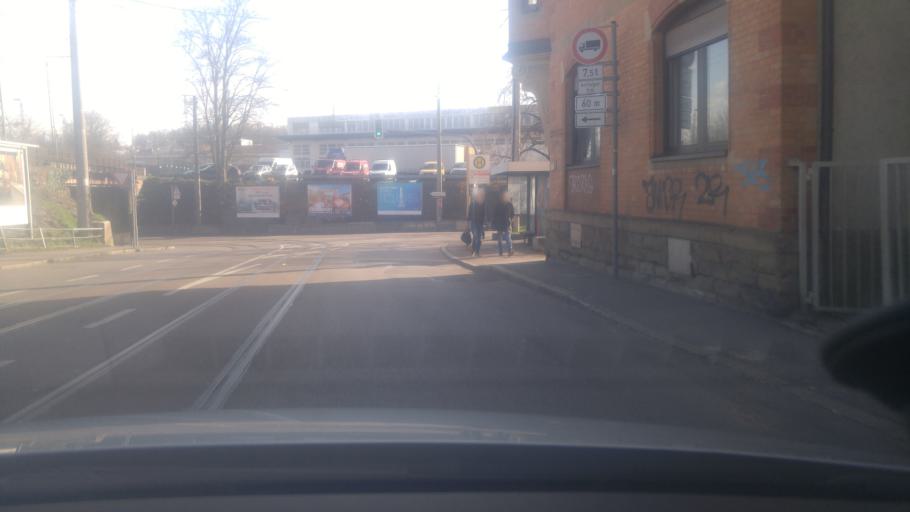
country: DE
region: Baden-Wuerttemberg
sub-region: Regierungsbezirk Stuttgart
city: Stuttgart Feuerbach
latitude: 48.8328
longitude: 9.1648
